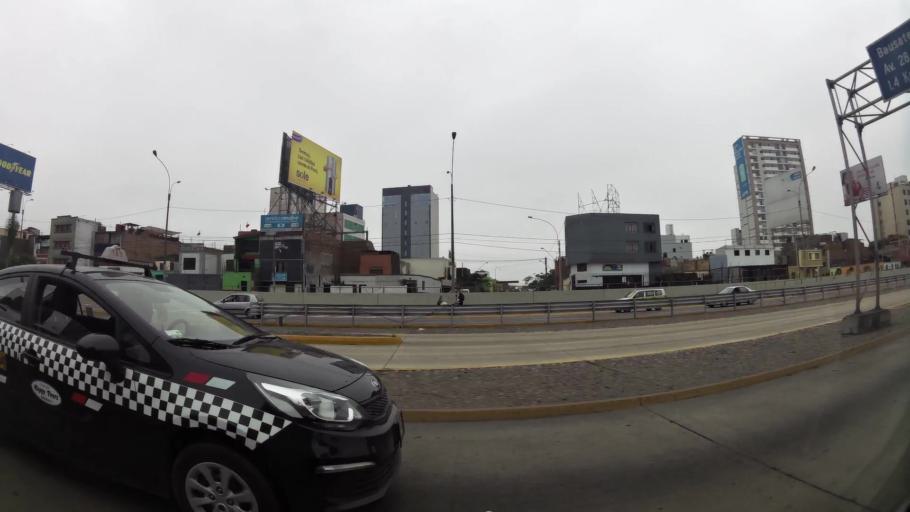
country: PE
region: Lima
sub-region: Lima
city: San Luis
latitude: -12.0802
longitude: -77.0273
